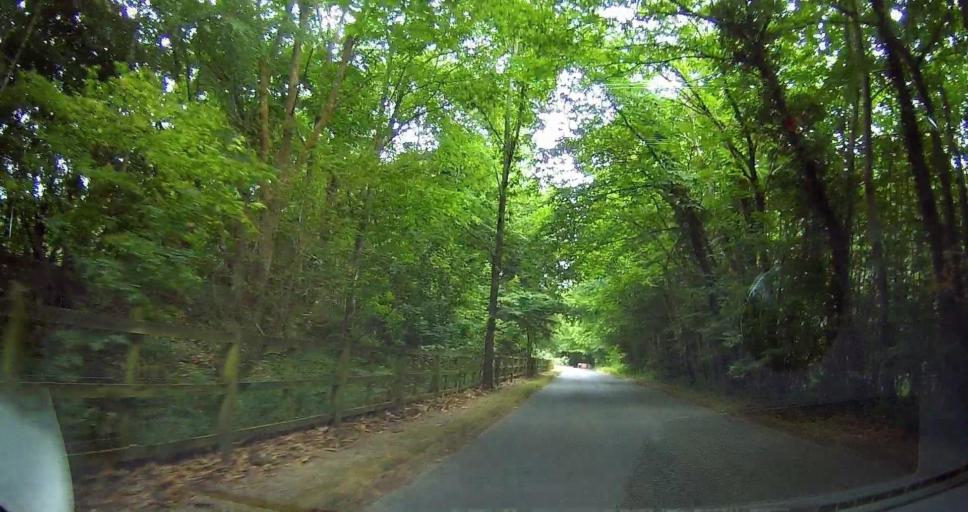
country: GB
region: England
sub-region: East Sussex
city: Wadhurst
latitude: 51.0830
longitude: 0.3932
